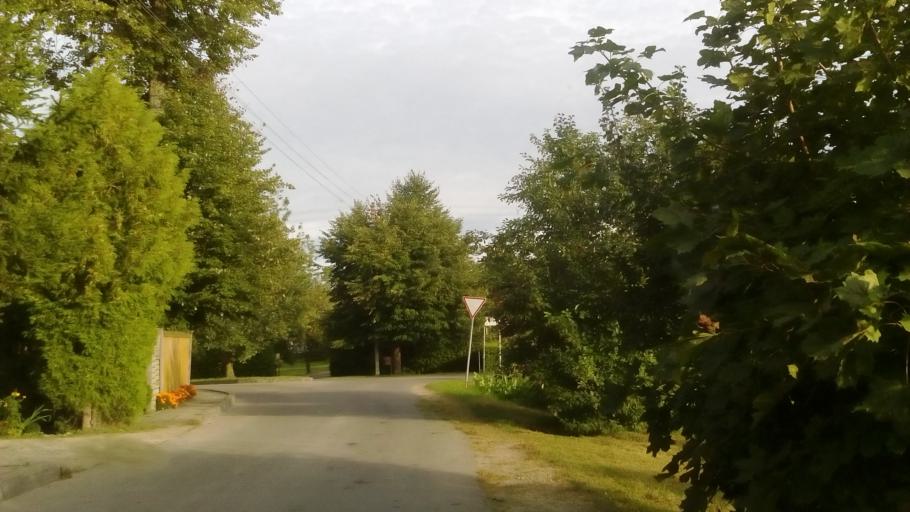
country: LT
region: Alytaus apskritis
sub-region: Alytus
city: Alytus
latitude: 54.3307
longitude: 23.8999
